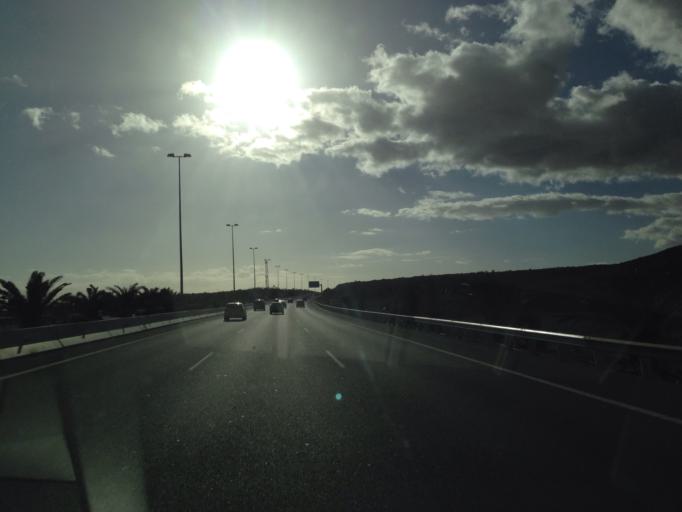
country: ES
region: Canary Islands
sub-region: Provincia de Las Palmas
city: Playa del Ingles
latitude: 27.7923
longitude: -15.4959
